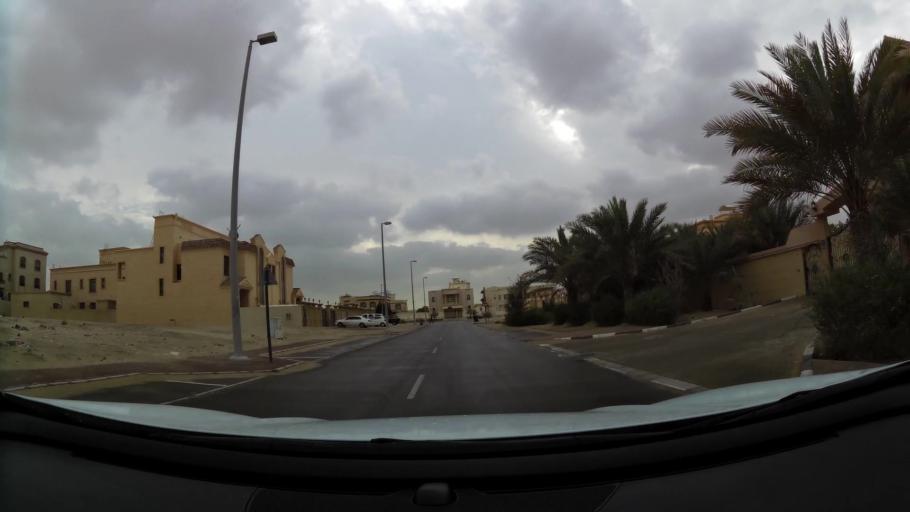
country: AE
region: Abu Dhabi
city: Abu Dhabi
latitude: 24.3516
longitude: 54.6365
